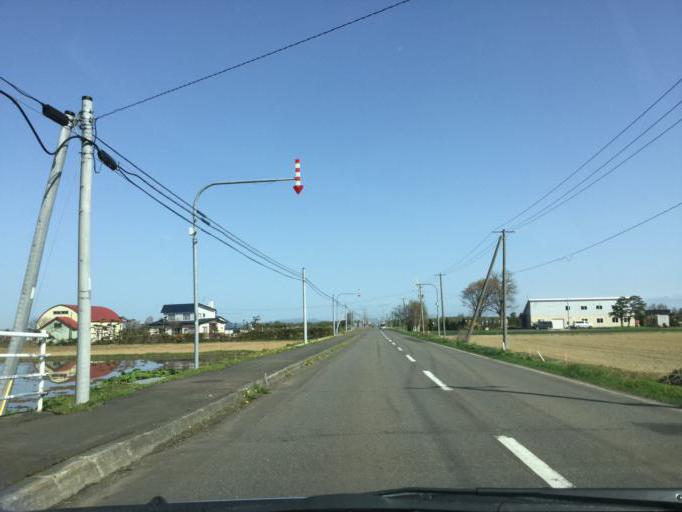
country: JP
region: Hokkaido
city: Iwamizawa
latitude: 43.1397
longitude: 141.7267
